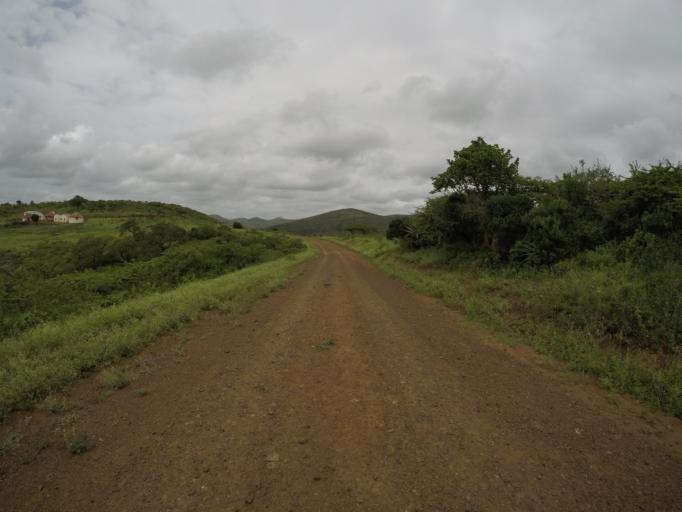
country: ZA
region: KwaZulu-Natal
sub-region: uThungulu District Municipality
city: Empangeni
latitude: -28.6264
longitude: 31.8885
